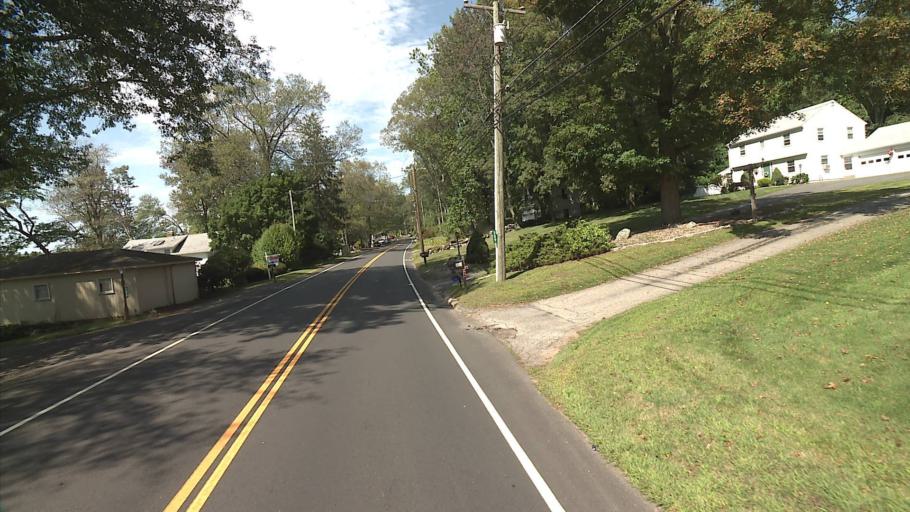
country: US
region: Connecticut
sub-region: Tolland County
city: South Coventry
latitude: 41.7133
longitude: -72.3176
